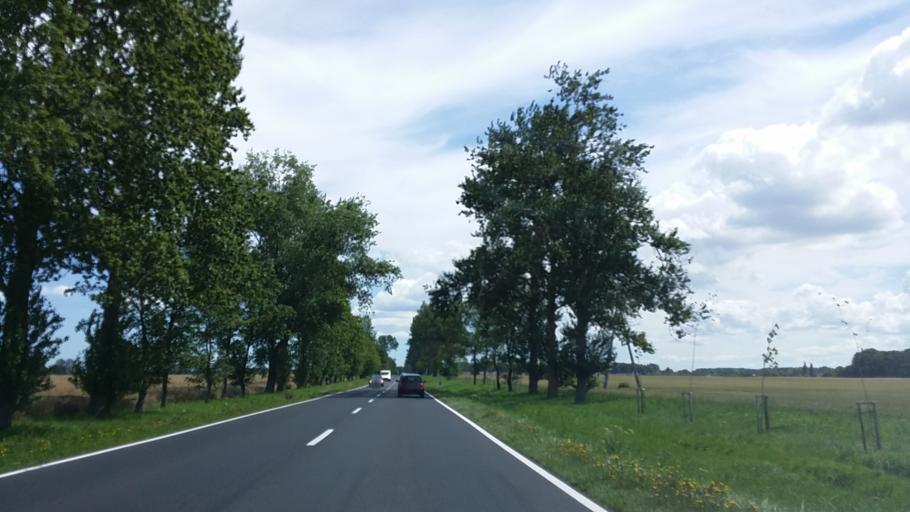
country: PL
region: West Pomeranian Voivodeship
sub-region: Powiat koszalinski
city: Mielno
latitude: 54.2224
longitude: 16.0578
